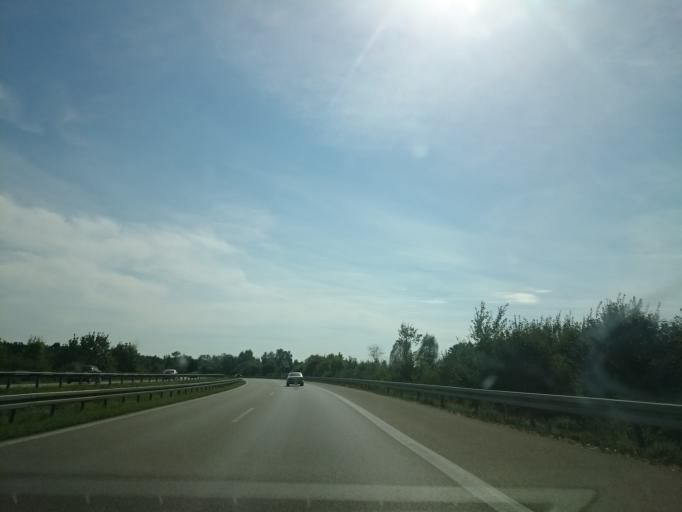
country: DE
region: Bavaria
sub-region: Swabia
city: Langweid
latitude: 48.4794
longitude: 10.8649
